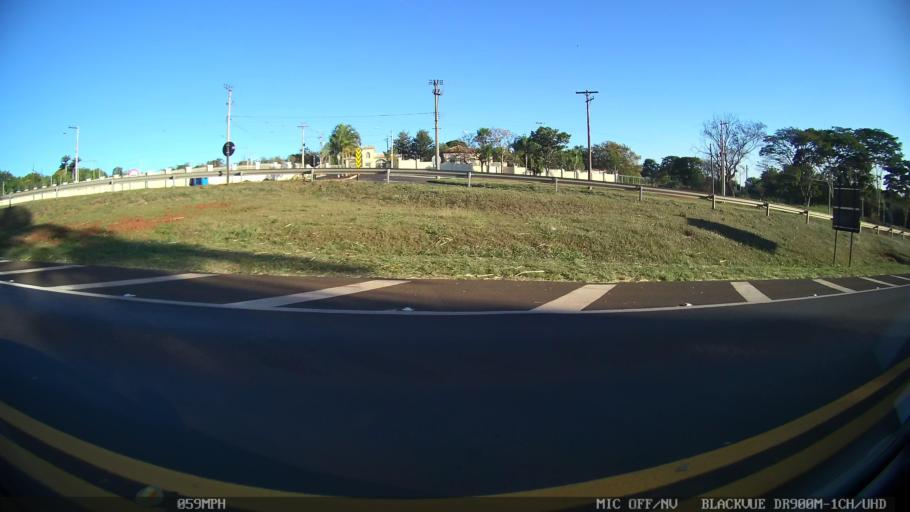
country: BR
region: Sao Paulo
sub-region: Araraquara
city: Araraquara
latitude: -21.8174
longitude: -48.1873
